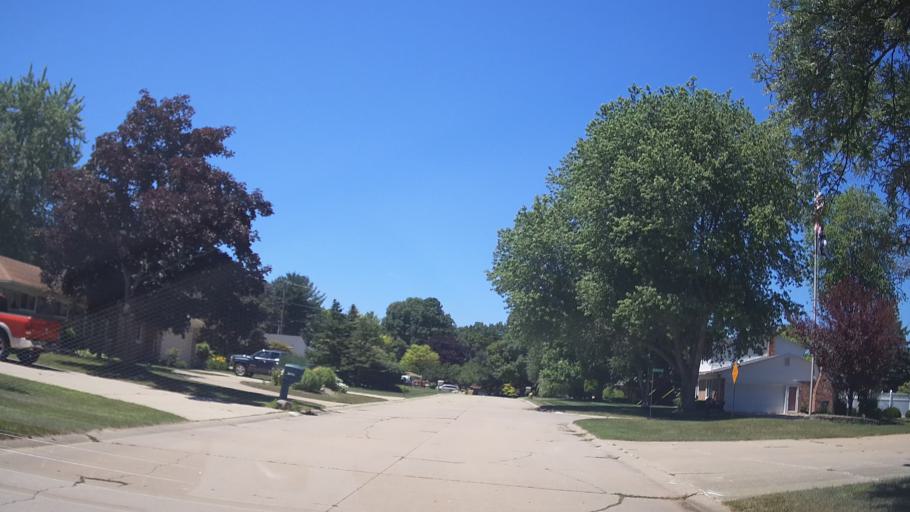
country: US
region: Michigan
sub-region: Macomb County
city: Clinton
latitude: 42.5861
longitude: -82.9178
